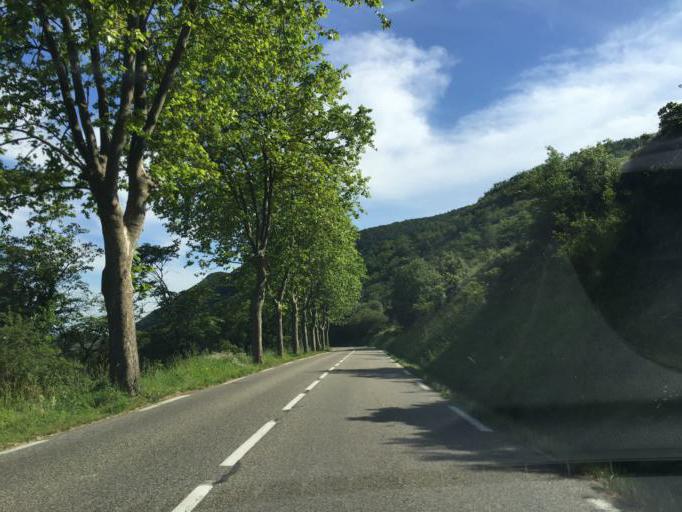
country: FR
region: Rhone-Alpes
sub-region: Departement de la Drome
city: Saulce-sur-Rhone
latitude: 44.7073
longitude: 4.7650
